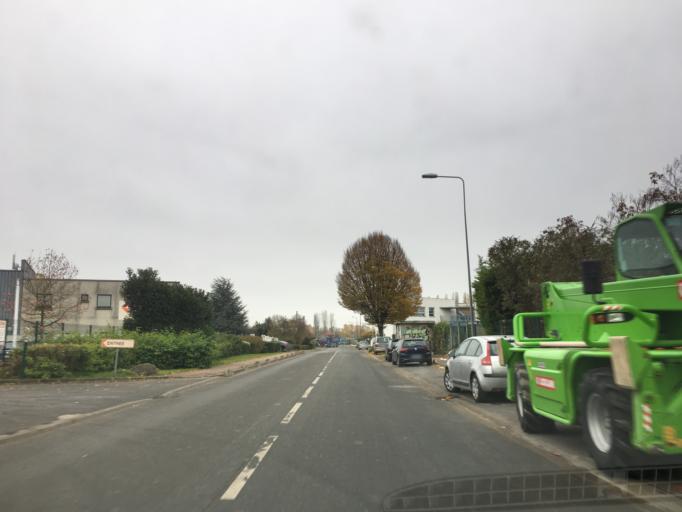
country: FR
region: Ile-de-France
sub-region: Departement du Val-de-Marne
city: Saint-Maur-des-Fosses
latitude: 48.7813
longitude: 2.5050
